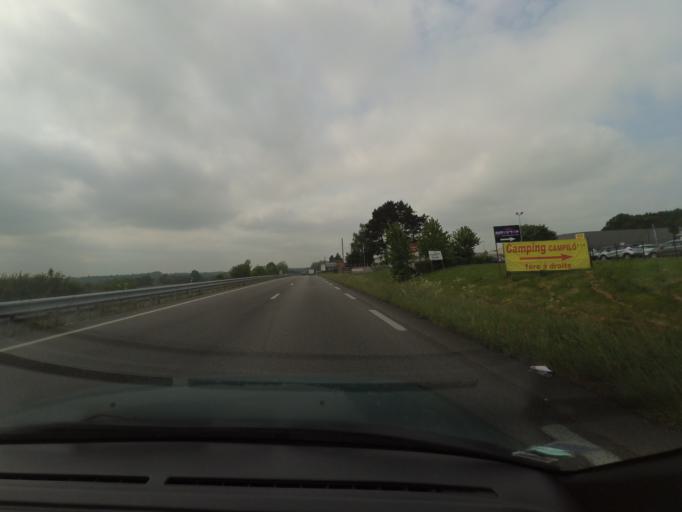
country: FR
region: Pays de la Loire
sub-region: Departement de la Vendee
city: Aubigny
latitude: 46.6208
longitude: -1.4431
